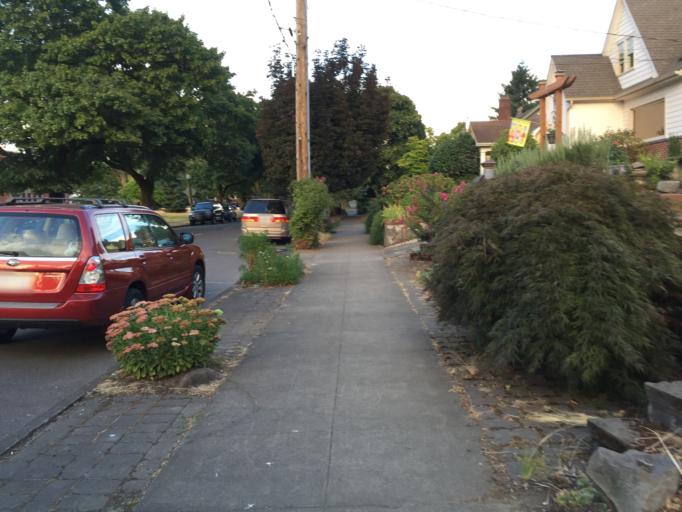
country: US
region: Oregon
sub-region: Multnomah County
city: Portland
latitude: 45.5378
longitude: -122.6282
